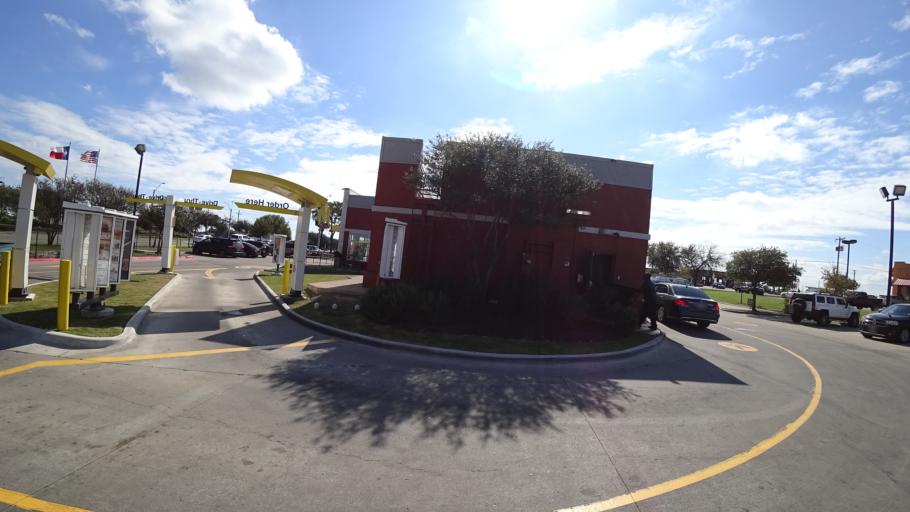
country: US
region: Texas
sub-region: Travis County
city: Windemere
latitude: 30.4481
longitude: -97.6397
